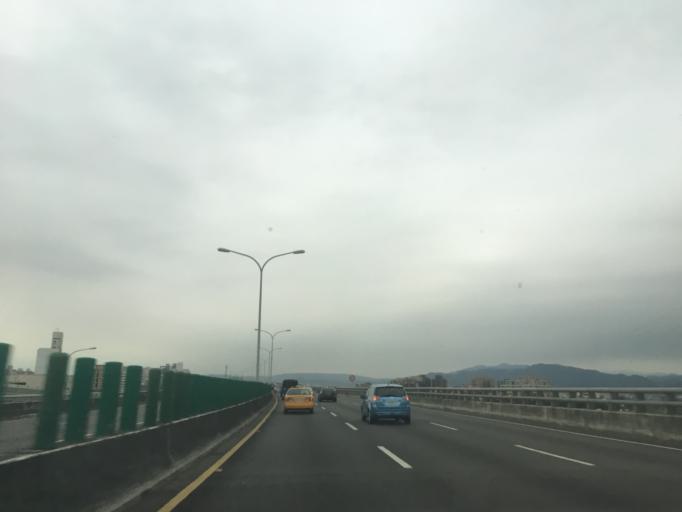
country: TW
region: Taiwan
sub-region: Taichung City
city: Taichung
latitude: 24.0958
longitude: 120.6891
